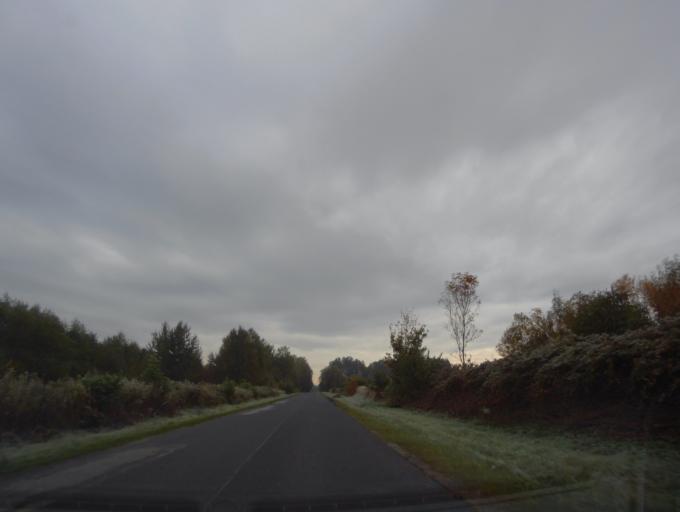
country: PL
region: Subcarpathian Voivodeship
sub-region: Powiat nizanski
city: Krzeszow
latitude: 50.4430
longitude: 22.3892
